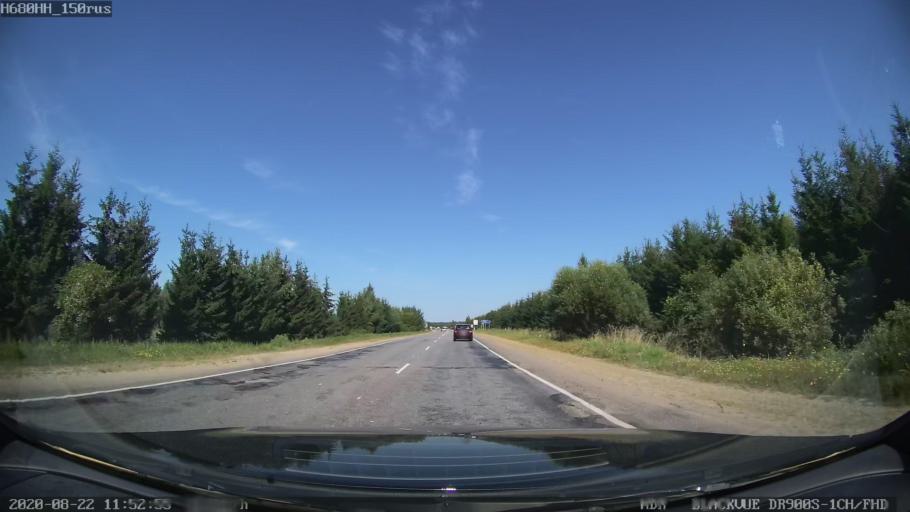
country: RU
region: Tverskaya
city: Vasil'yevskiy Mokh
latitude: 57.1211
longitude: 36.1141
